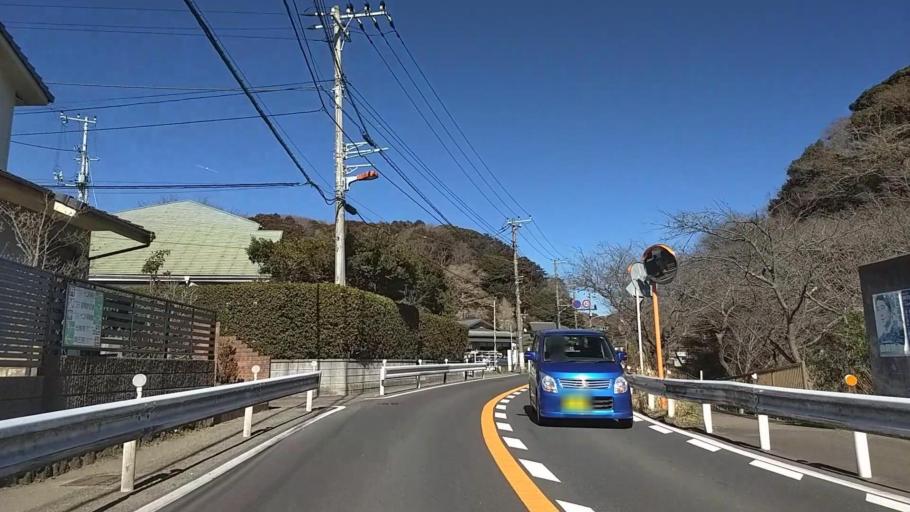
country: JP
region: Kanagawa
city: Zushi
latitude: 35.3221
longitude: 139.5805
